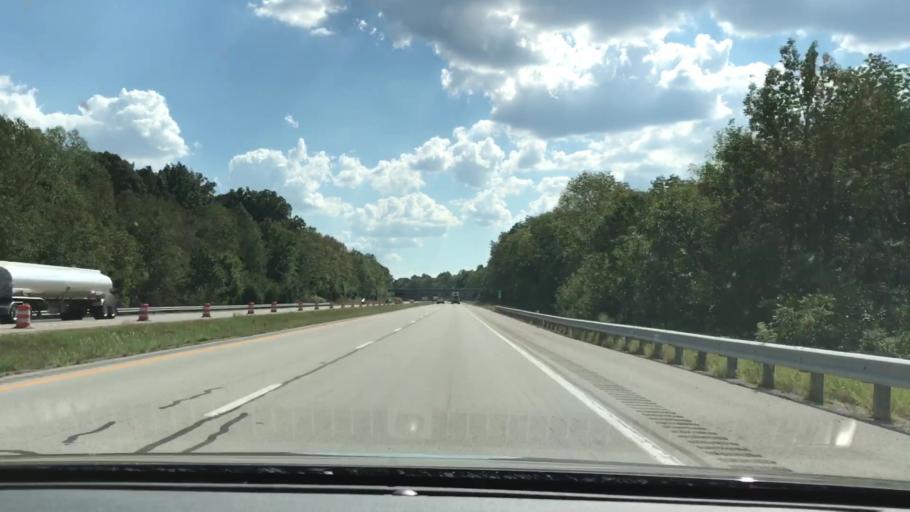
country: US
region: Kentucky
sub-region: Ohio County
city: Oak Grove
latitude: 37.2715
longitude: -86.7470
